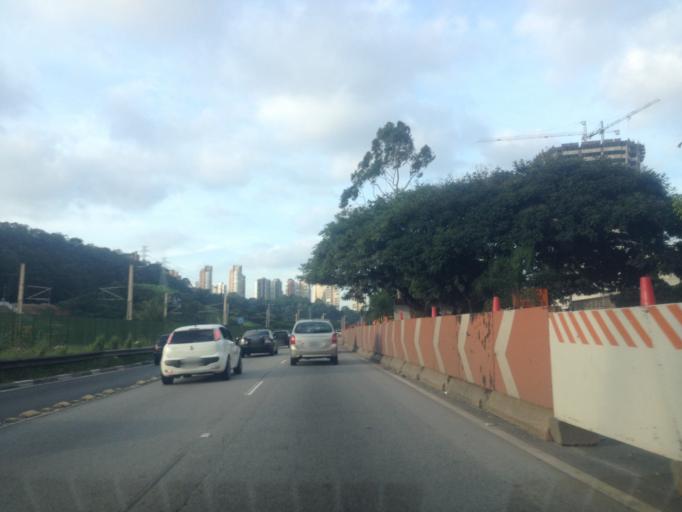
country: BR
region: Sao Paulo
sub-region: Taboao Da Serra
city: Taboao da Serra
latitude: -23.6430
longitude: -46.7250
